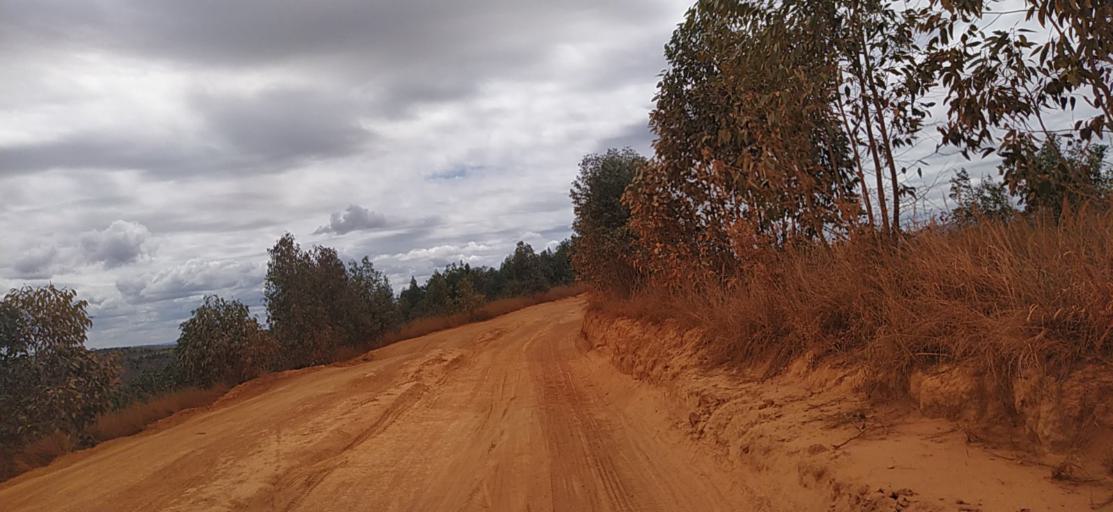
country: MG
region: Alaotra Mangoro
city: Ambatondrazaka
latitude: -18.0462
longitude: 48.2490
